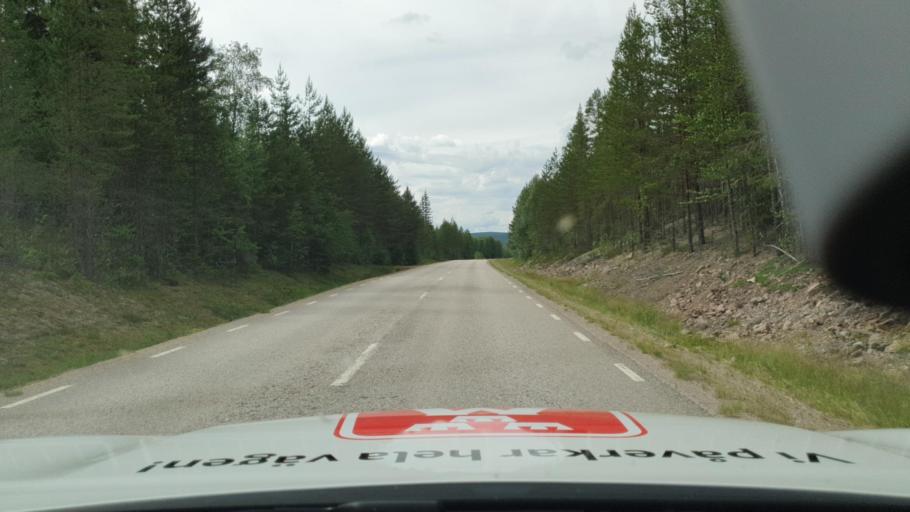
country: NO
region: Hedmark
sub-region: Trysil
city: Innbygda
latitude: 60.9310
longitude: 12.4996
